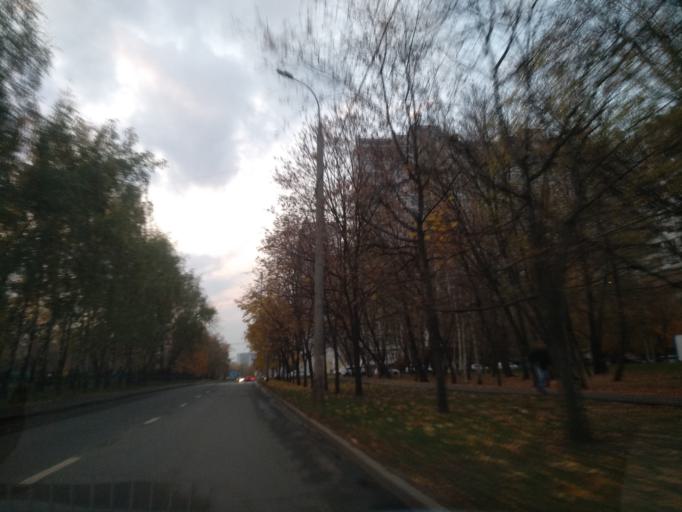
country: RU
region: Moscow
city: Leonovo
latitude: 55.8647
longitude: 37.6541
